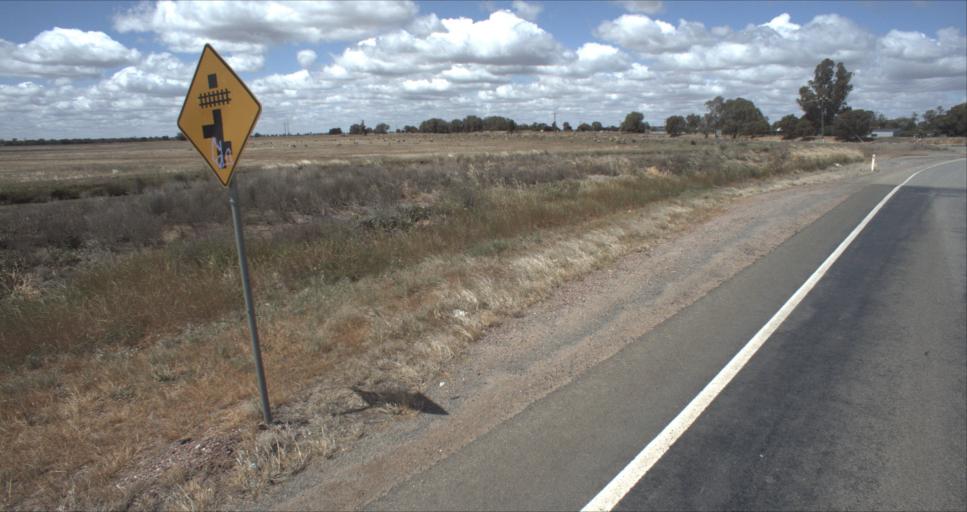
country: AU
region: New South Wales
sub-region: Murrumbidgee Shire
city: Darlington Point
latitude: -34.5160
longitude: 146.1855
